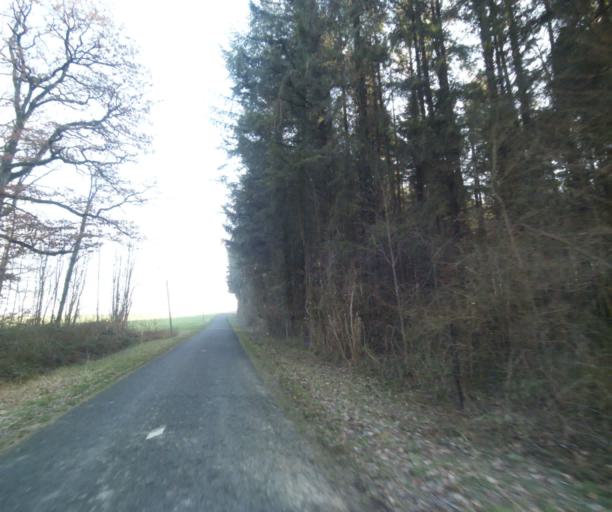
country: FR
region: Champagne-Ardenne
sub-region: Departement de la Haute-Marne
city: Bienville
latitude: 48.4984
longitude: 5.0552
